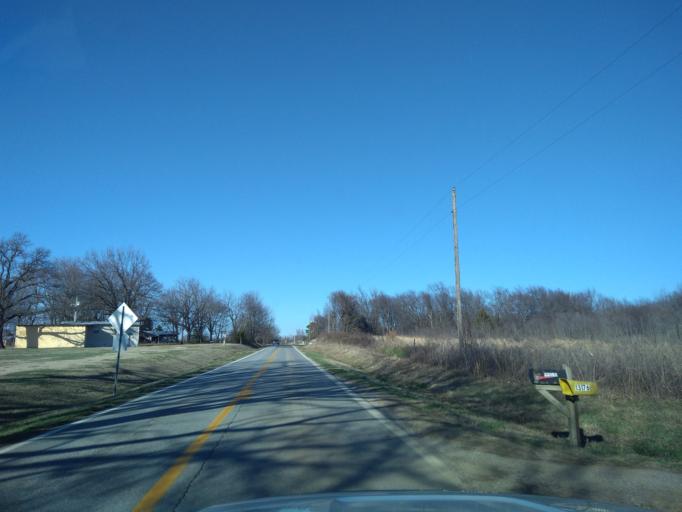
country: US
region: Arkansas
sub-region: Washington County
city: Lincoln
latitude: 35.9296
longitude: -94.3862
